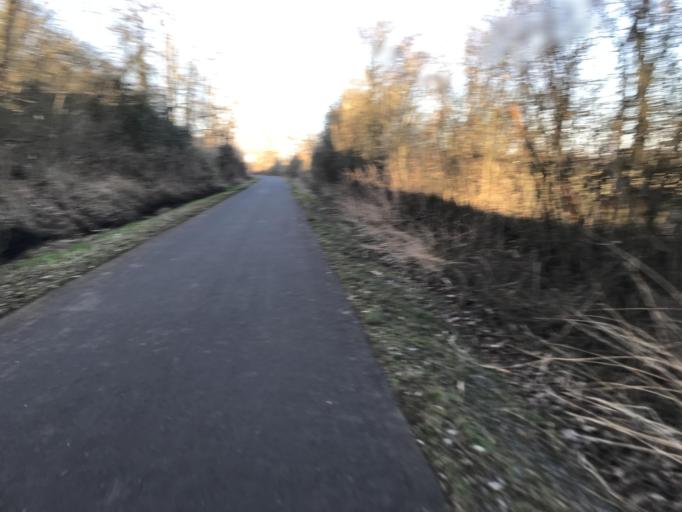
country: DE
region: Hesse
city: Schwalmstadt
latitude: 50.9021
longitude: 9.2374
